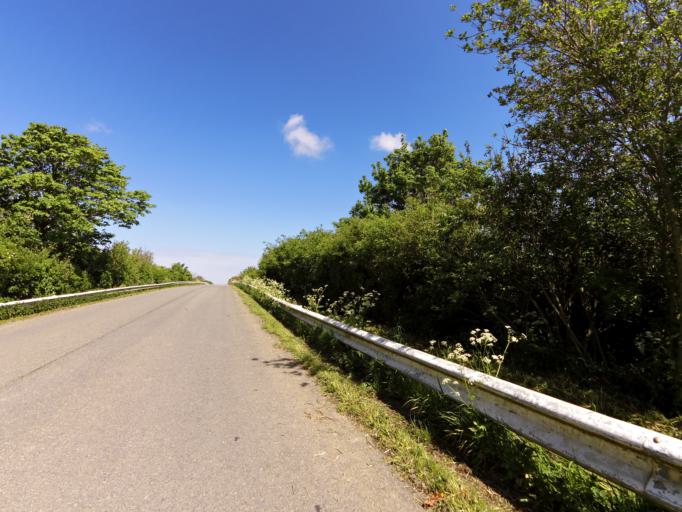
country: BE
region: Flanders
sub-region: Provincie West-Vlaanderen
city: Middelkerke
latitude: 51.1373
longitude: 2.8438
